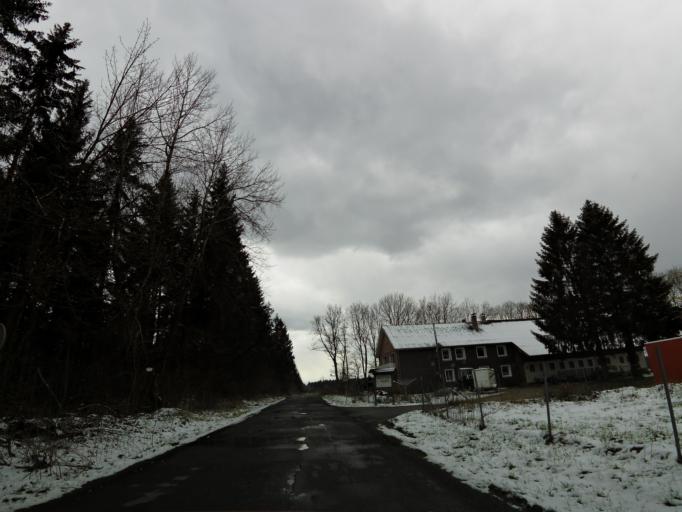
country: DE
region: Lower Saxony
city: Clausthal-Zellerfeld
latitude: 51.7915
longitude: 10.3644
